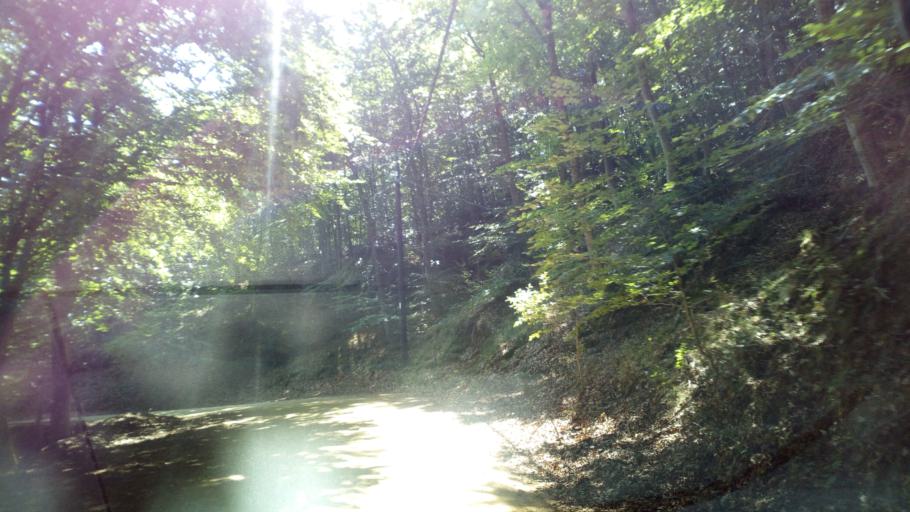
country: GR
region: Central Macedonia
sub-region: Nomos Thessalonikis
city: Sochos
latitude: 40.8290
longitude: 23.3375
